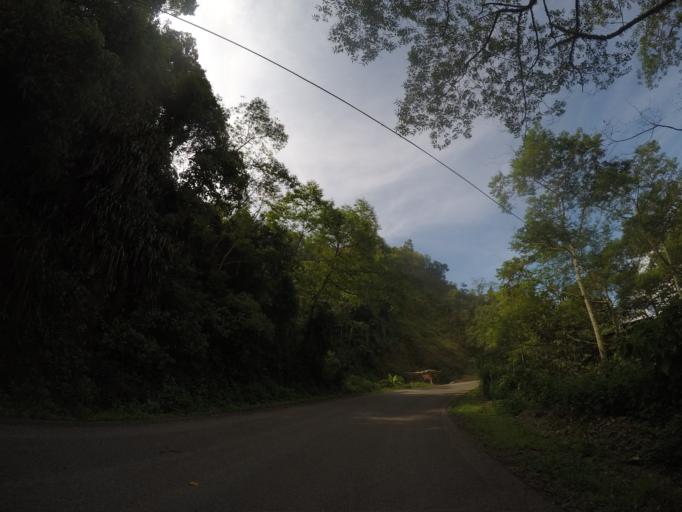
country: MX
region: Oaxaca
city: Pluma Hidalgo
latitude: 15.9323
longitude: -96.4232
